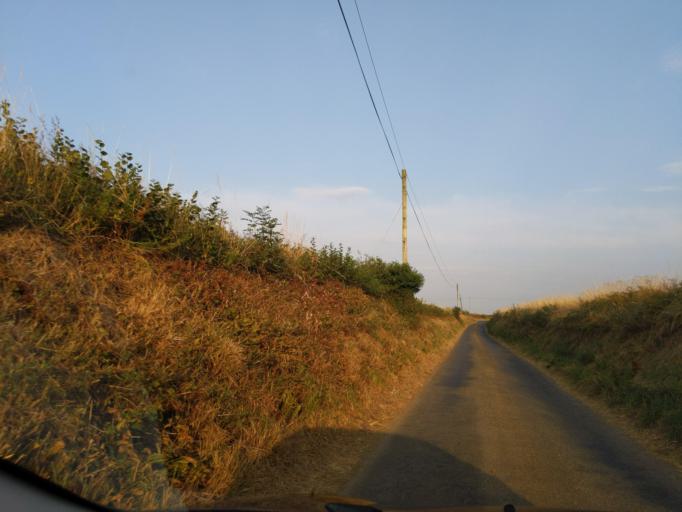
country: GB
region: England
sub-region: Cornwall
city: Fowey
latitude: 50.3675
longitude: -4.5864
